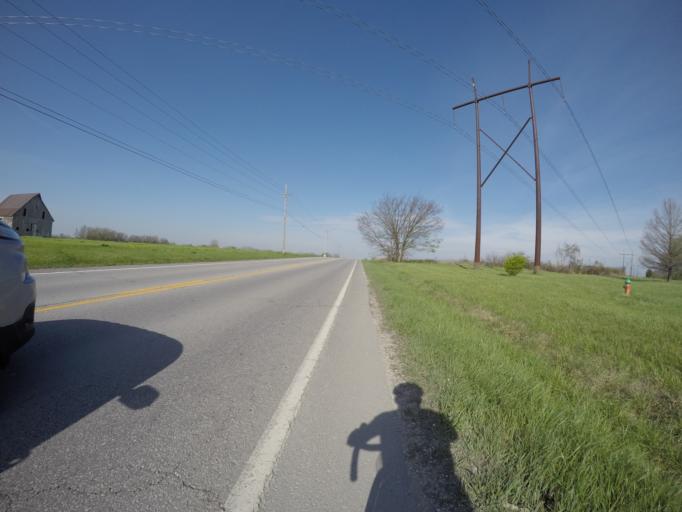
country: US
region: Missouri
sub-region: Cass County
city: Lake Winnebago
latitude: 38.8523
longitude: -94.3666
